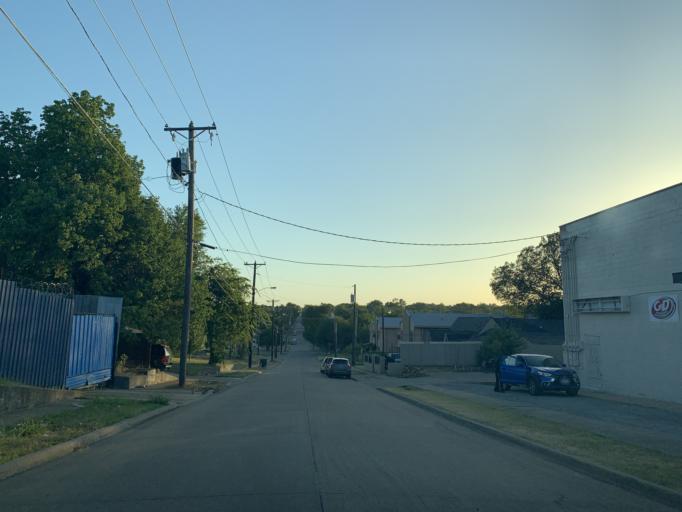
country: US
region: Texas
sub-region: Dallas County
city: Dallas
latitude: 32.7026
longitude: -96.7984
